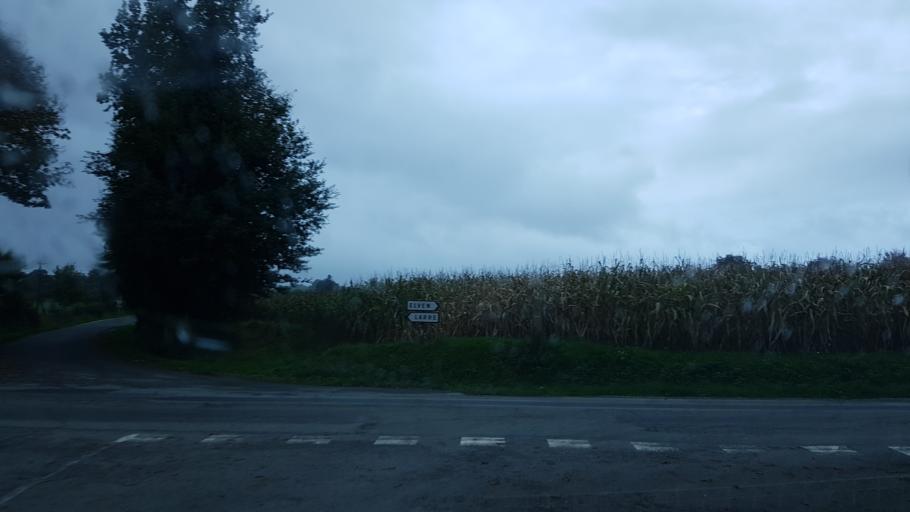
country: FR
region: Brittany
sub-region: Departement du Morbihan
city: Elven
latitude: 47.7329
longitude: -2.5748
